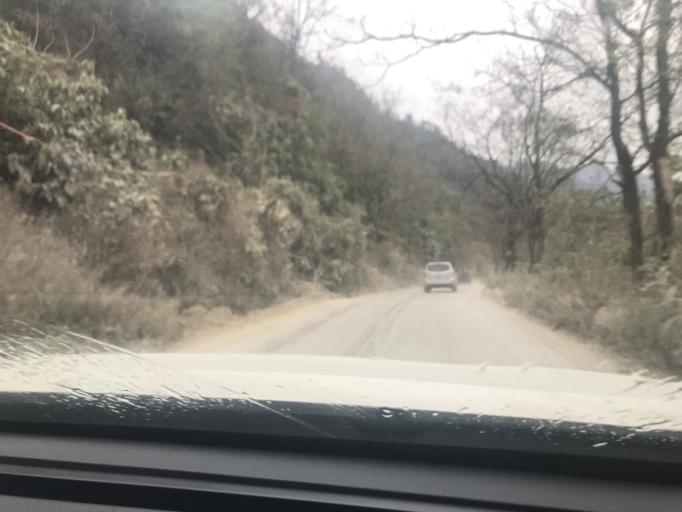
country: CN
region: Guangxi Zhuangzu Zizhiqu
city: Xinzhou
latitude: 24.9907
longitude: 105.8238
